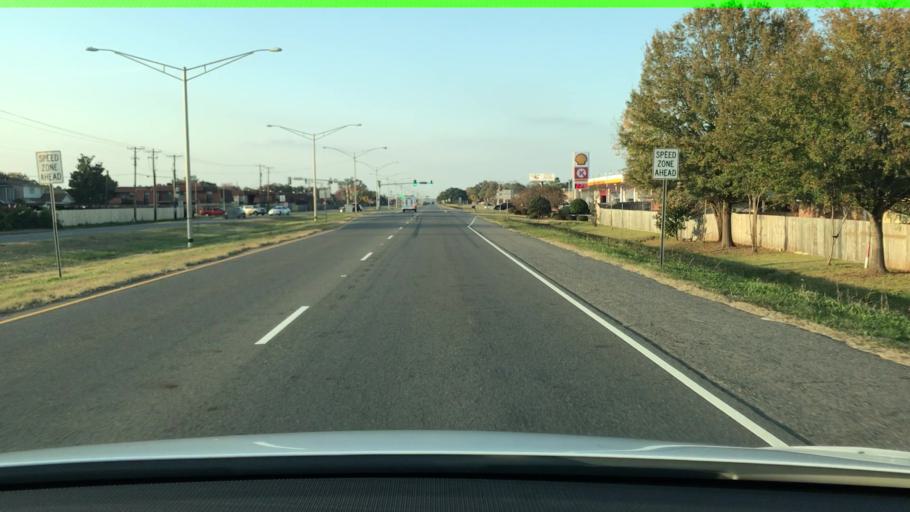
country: US
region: Louisiana
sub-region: Bossier Parish
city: Bossier City
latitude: 32.4115
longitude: -93.7000
